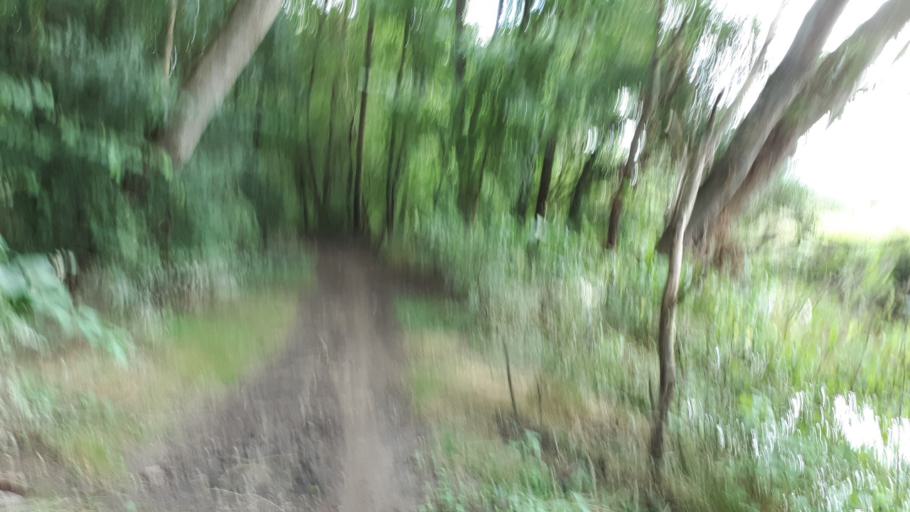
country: FR
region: Pays de la Loire
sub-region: Departement de Maine-et-Loire
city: La Possonniere
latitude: 47.3369
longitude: -0.6956
